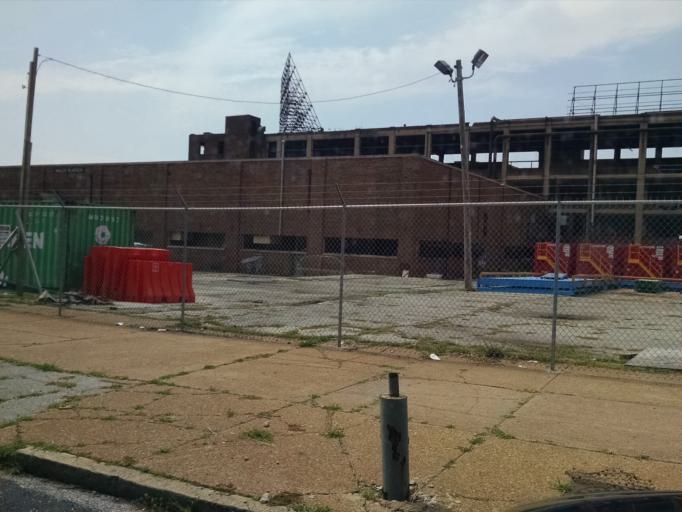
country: US
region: Missouri
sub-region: City of Saint Louis
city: St. Louis
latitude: 38.6558
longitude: -90.2207
